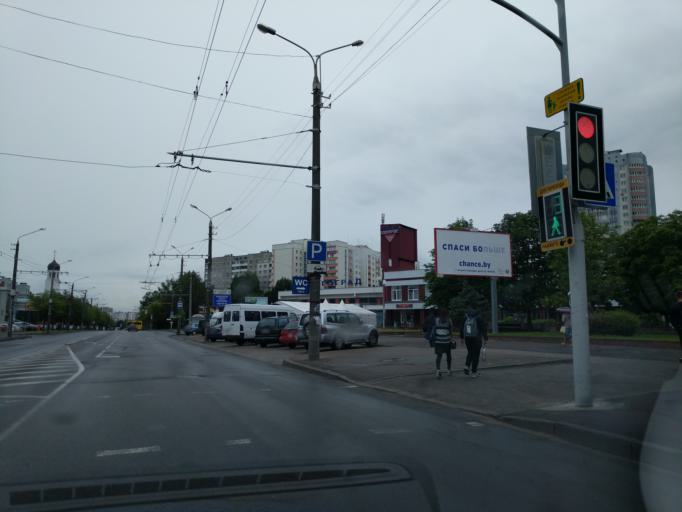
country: BY
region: Minsk
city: Novoye Medvezhino
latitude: 53.8620
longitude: 27.4787
